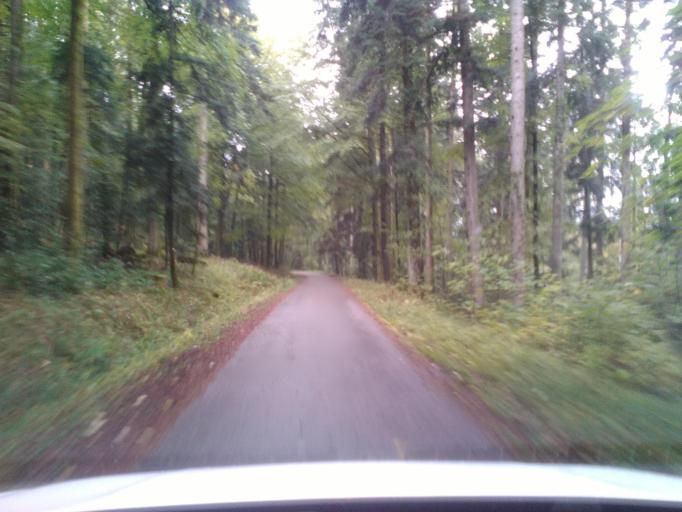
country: FR
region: Lorraine
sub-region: Departement des Vosges
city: Sainte-Marguerite
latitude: 48.3213
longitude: 7.0061
